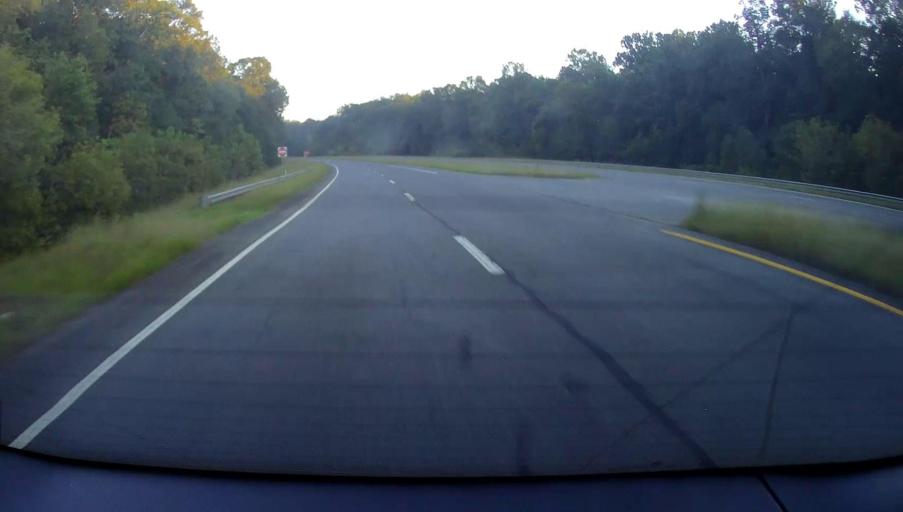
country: US
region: Georgia
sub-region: Houston County
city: Perry
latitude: 32.3999
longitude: -83.6427
